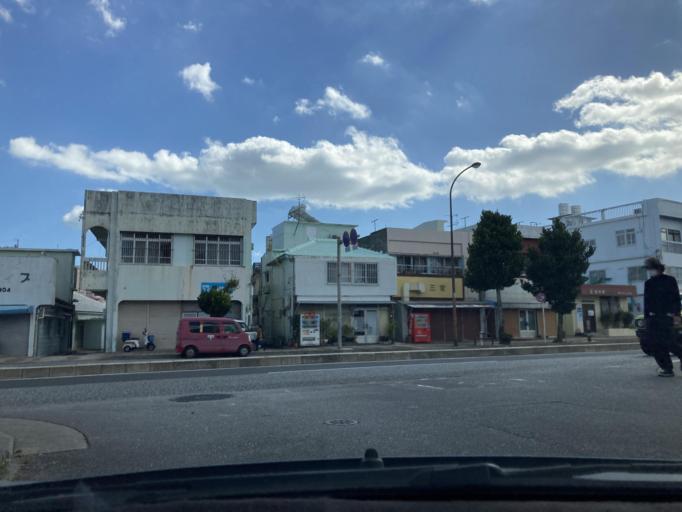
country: JP
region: Okinawa
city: Okinawa
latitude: 26.3256
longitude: 127.7929
